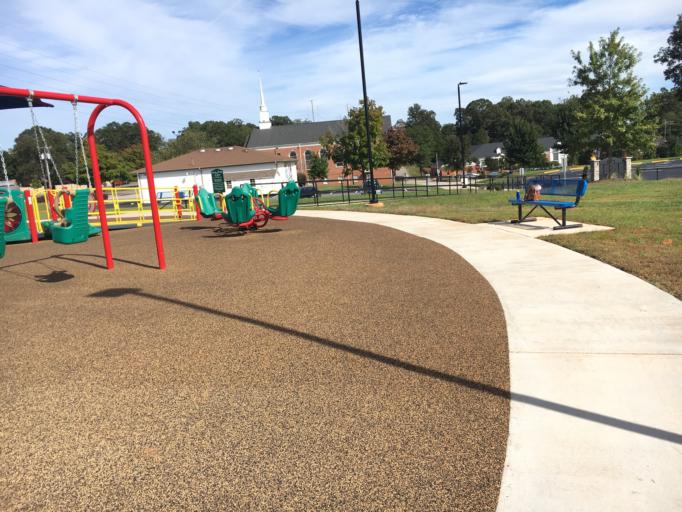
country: US
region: South Carolina
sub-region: Spartanburg County
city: Lyman
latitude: 34.9485
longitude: -82.1243
